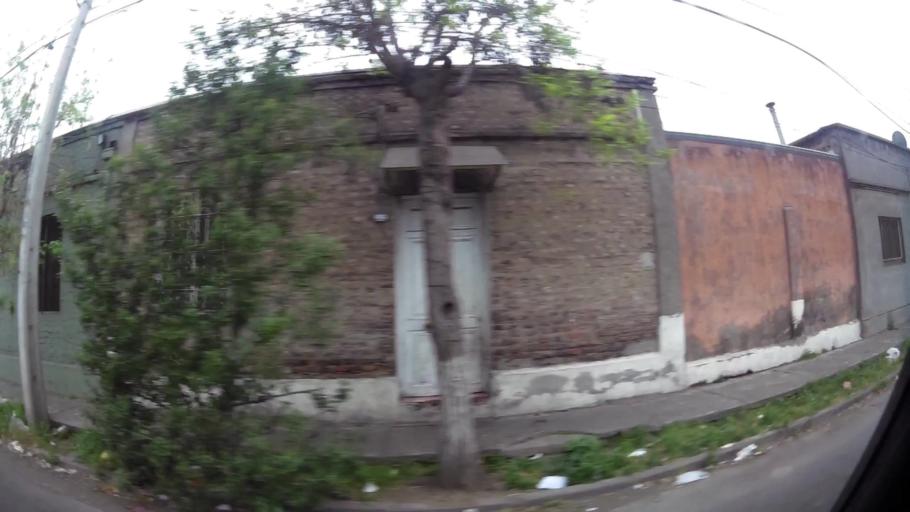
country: CL
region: Santiago Metropolitan
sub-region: Provincia de Santiago
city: Santiago
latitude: -33.4943
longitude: -70.6424
